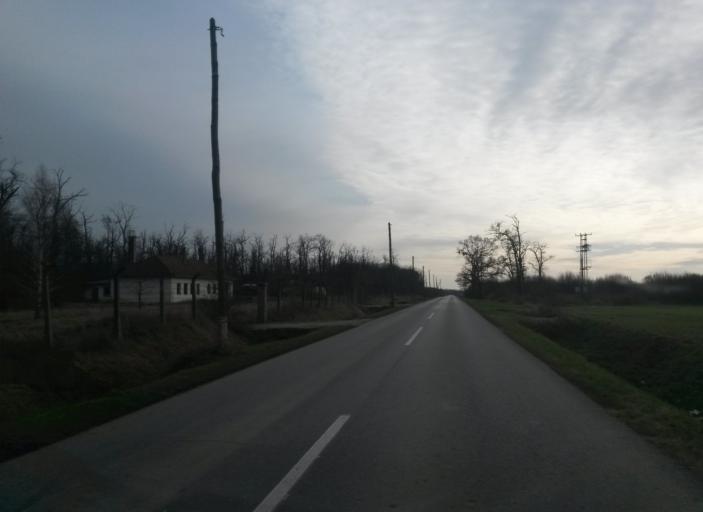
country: HR
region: Osjecko-Baranjska
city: Ovcara
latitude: 45.5147
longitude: 18.5935
